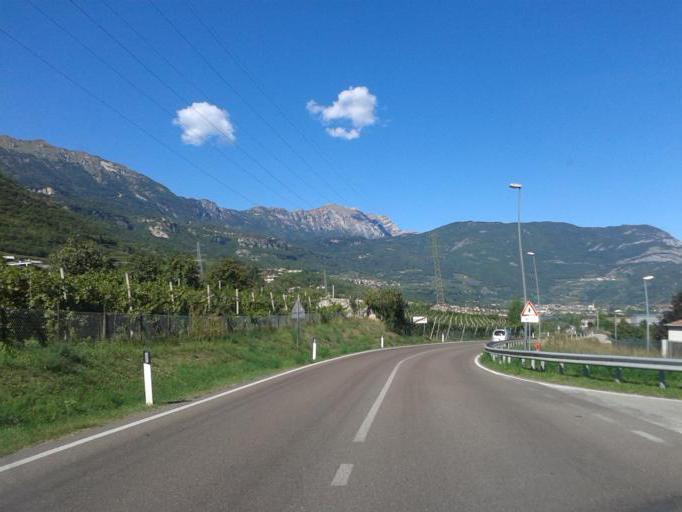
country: IT
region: Trentino-Alto Adige
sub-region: Provincia di Trento
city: Isera
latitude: 45.8847
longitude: 11.0125
